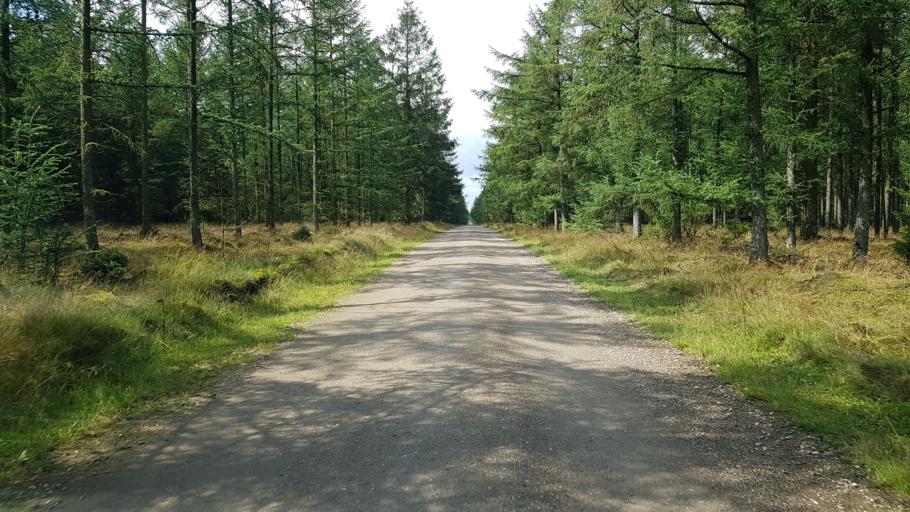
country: DK
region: South Denmark
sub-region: Vejen Kommune
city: Holsted
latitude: 55.5953
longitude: 8.9015
